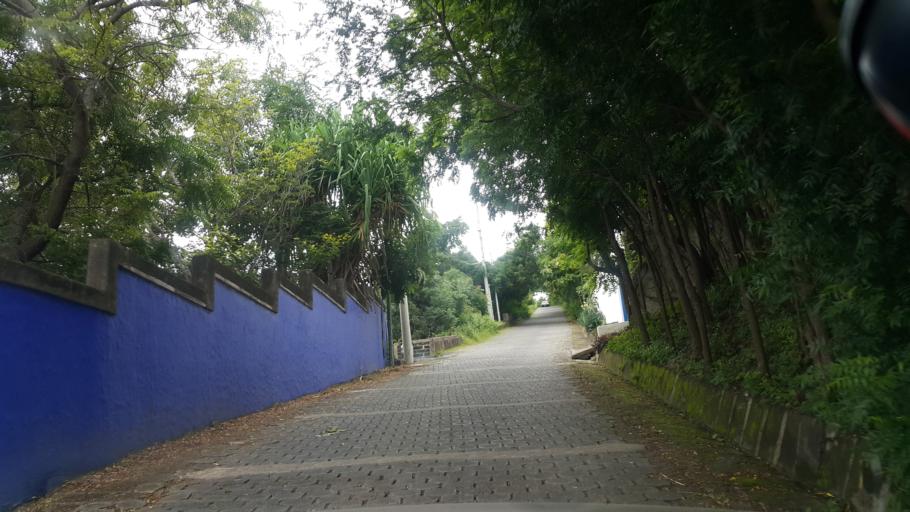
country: NI
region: Rivas
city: San Juan del Sur
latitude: 11.2636
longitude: -85.8800
